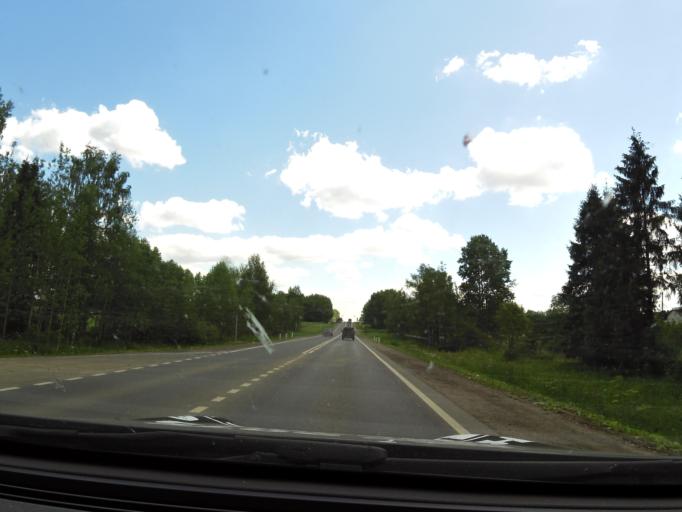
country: RU
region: Vologda
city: Molochnoye
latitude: 59.2633
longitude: 39.7428
